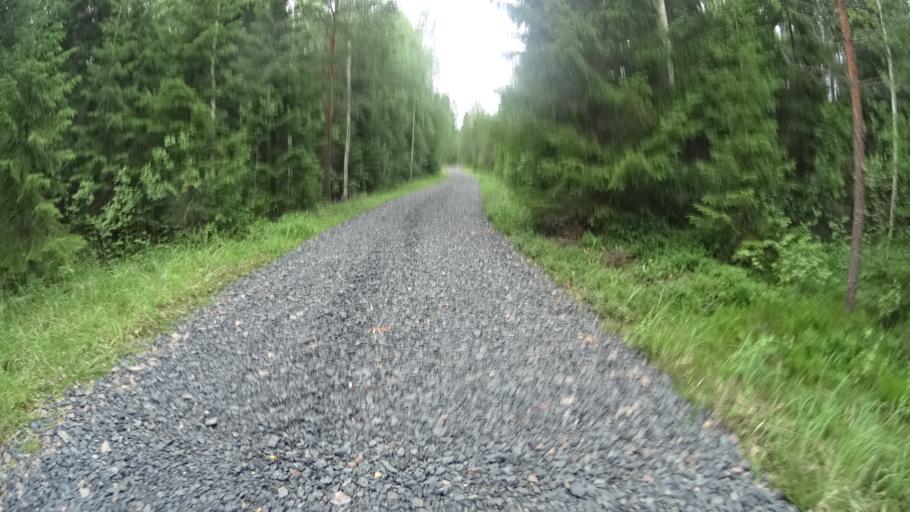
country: FI
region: Uusimaa
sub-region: Helsinki
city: Karkkila
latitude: 60.5853
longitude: 24.1565
